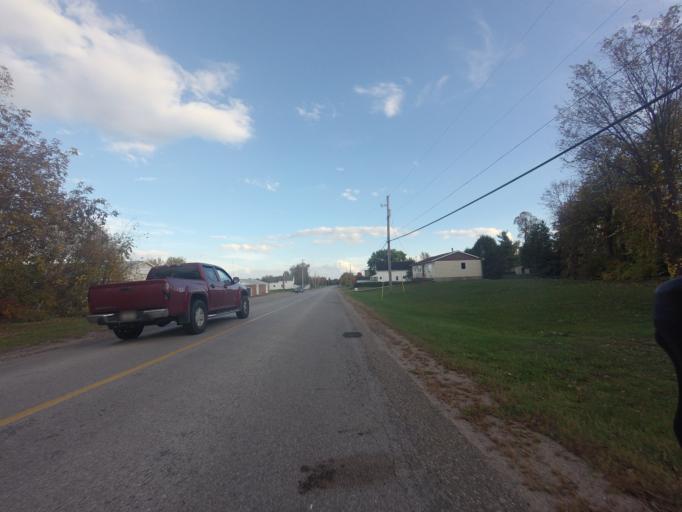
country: CA
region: Ontario
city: Pembroke
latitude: 45.5326
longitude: -77.0915
